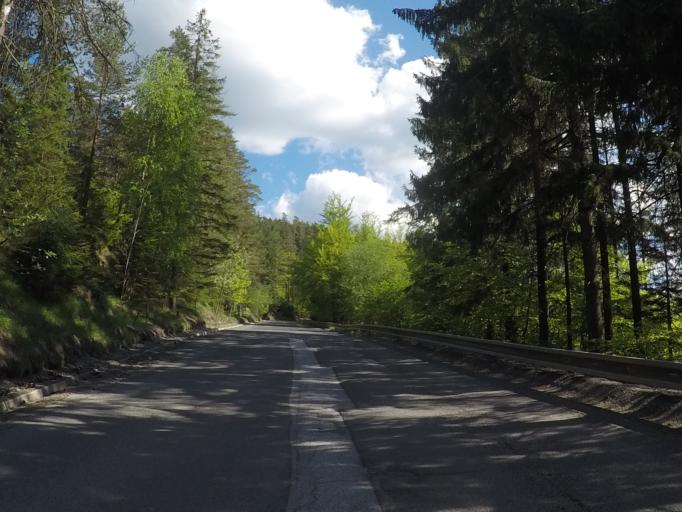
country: SK
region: Kosicky
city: Dobsina
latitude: 48.9096
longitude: 20.2560
